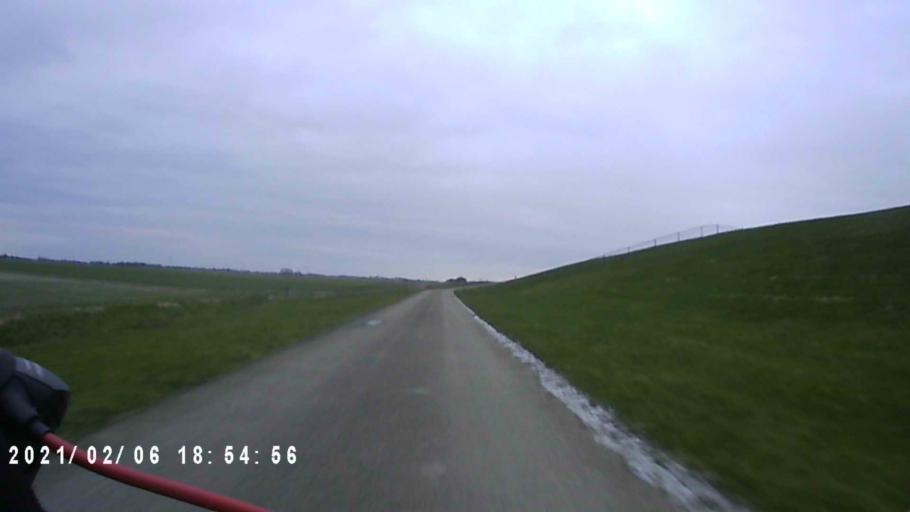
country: NL
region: Groningen
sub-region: Gemeente Winsum
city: Winsum
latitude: 53.4241
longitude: 6.5288
